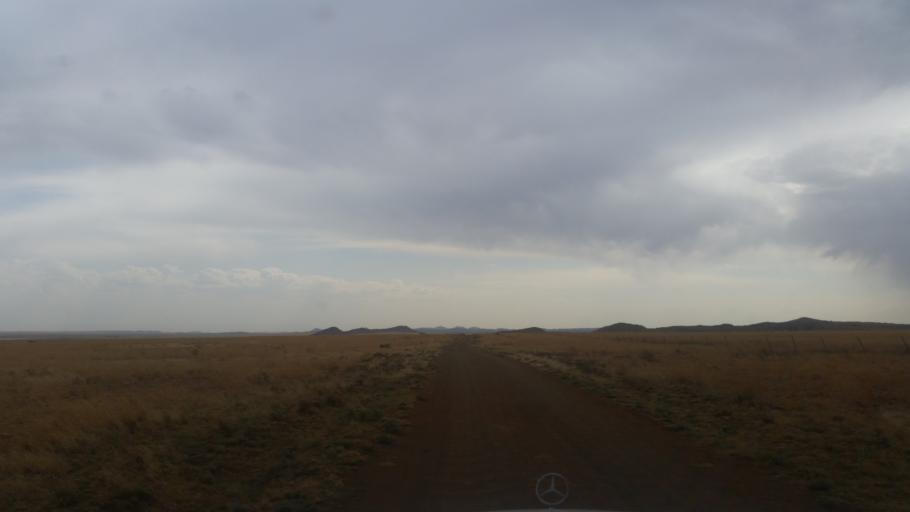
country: ZA
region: Orange Free State
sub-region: Xhariep District Municipality
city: Trompsburg
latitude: -30.5069
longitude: 25.9291
